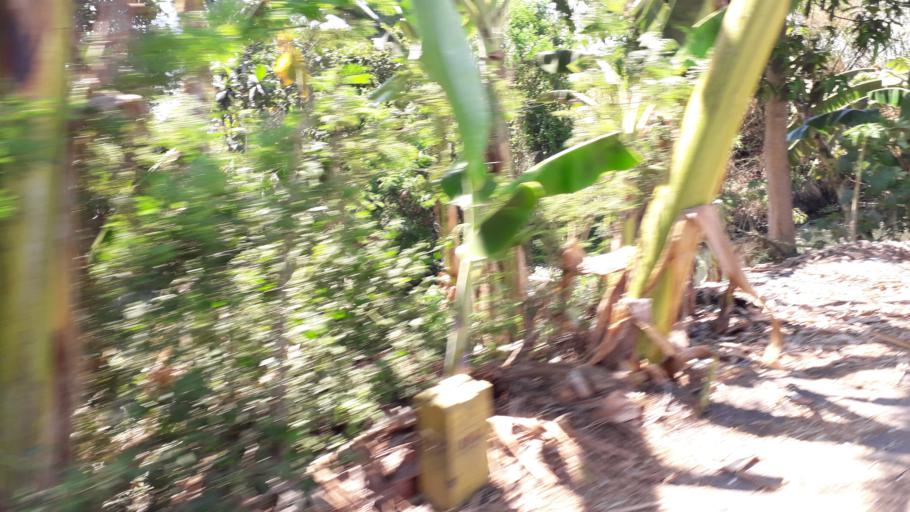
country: ID
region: Daerah Istimewa Yogyakarta
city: Pundong
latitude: -7.9458
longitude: 110.3296
